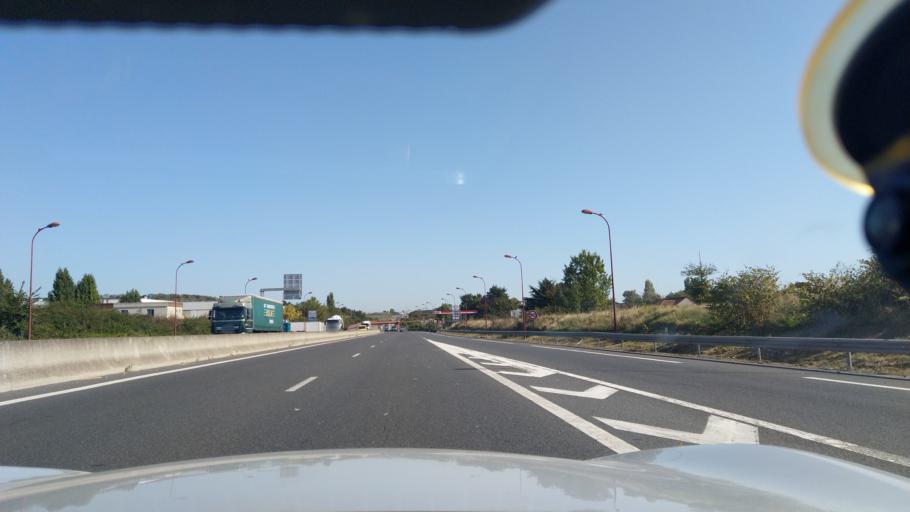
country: FR
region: Ile-de-France
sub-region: Departement du Val-d'Oise
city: Gonesse
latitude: 48.9796
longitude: 2.4660
